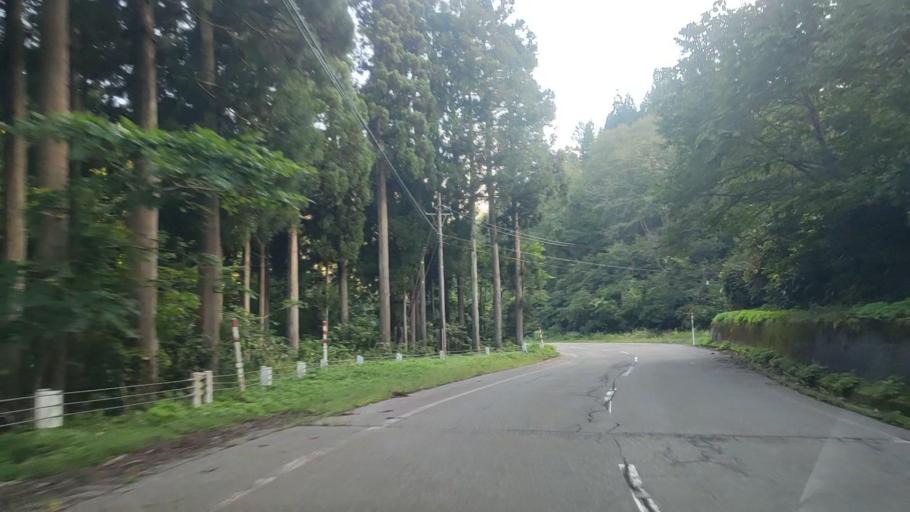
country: JP
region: Toyama
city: Yatsuomachi-higashikumisaka
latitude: 36.4897
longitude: 137.0499
